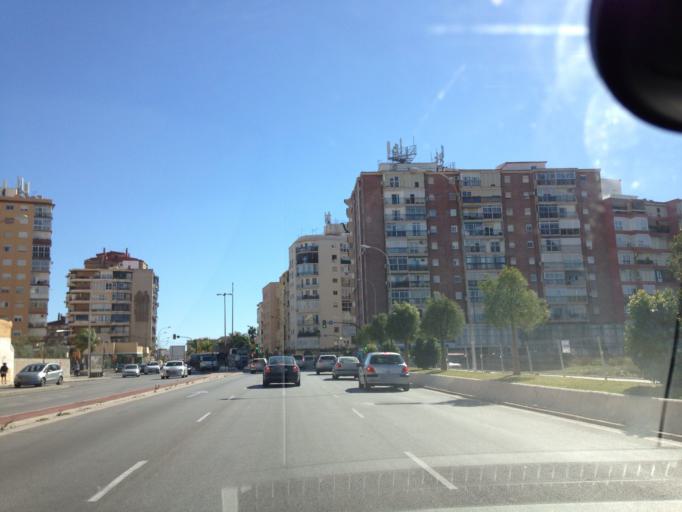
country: ES
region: Andalusia
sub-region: Provincia de Malaga
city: Malaga
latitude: 36.7047
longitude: -4.4415
